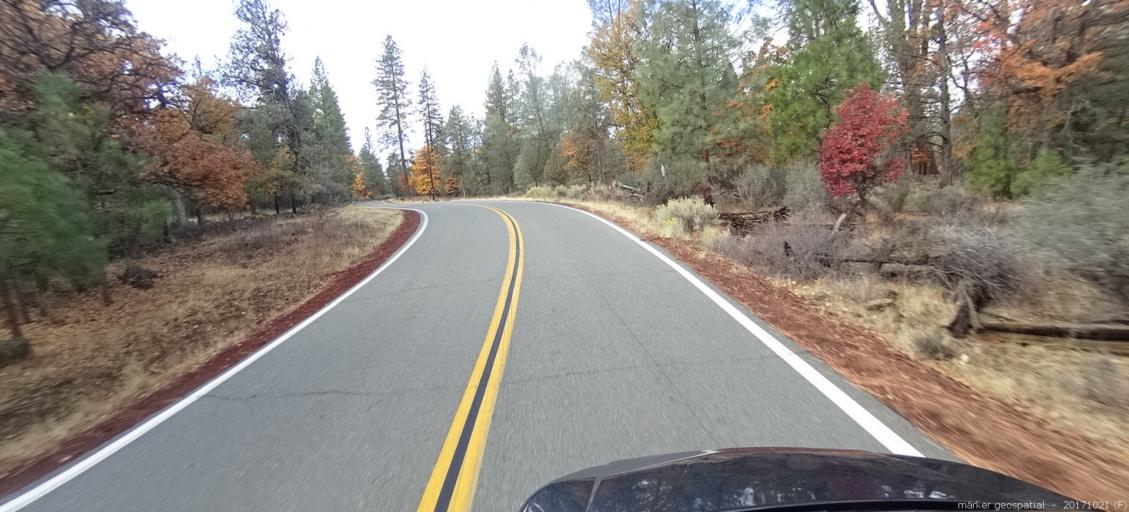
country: US
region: California
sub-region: Shasta County
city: Burney
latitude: 40.9191
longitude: -121.5396
